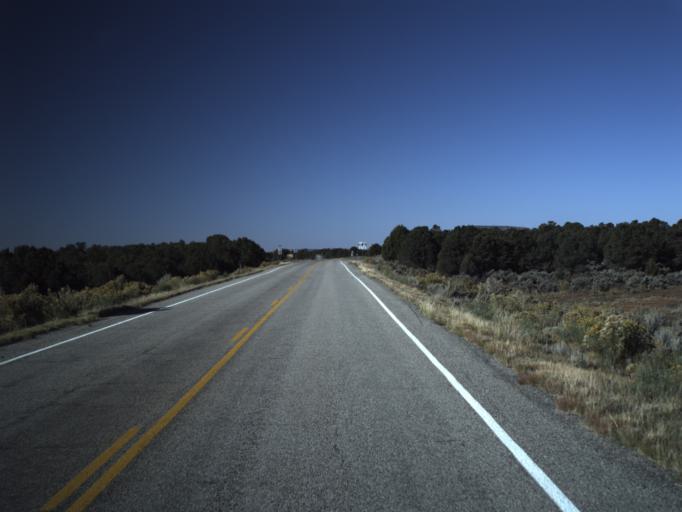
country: US
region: Utah
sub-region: San Juan County
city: Blanding
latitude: 37.5824
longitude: -109.9119
